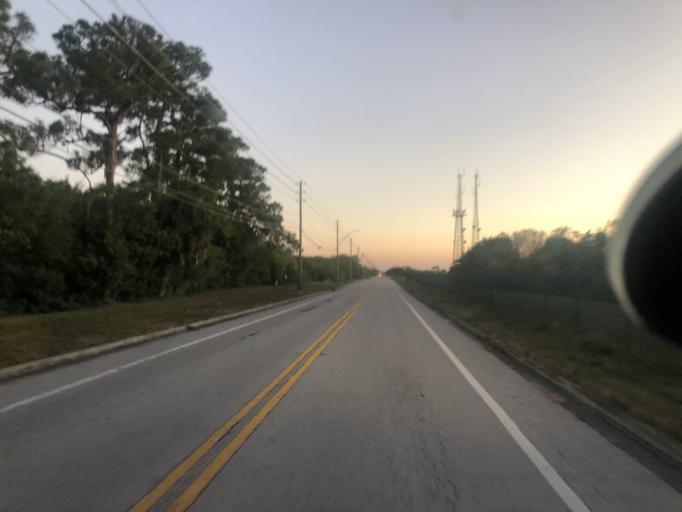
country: US
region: Florida
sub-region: Pinellas County
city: Feather Sound
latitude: 27.8715
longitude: -82.6553
